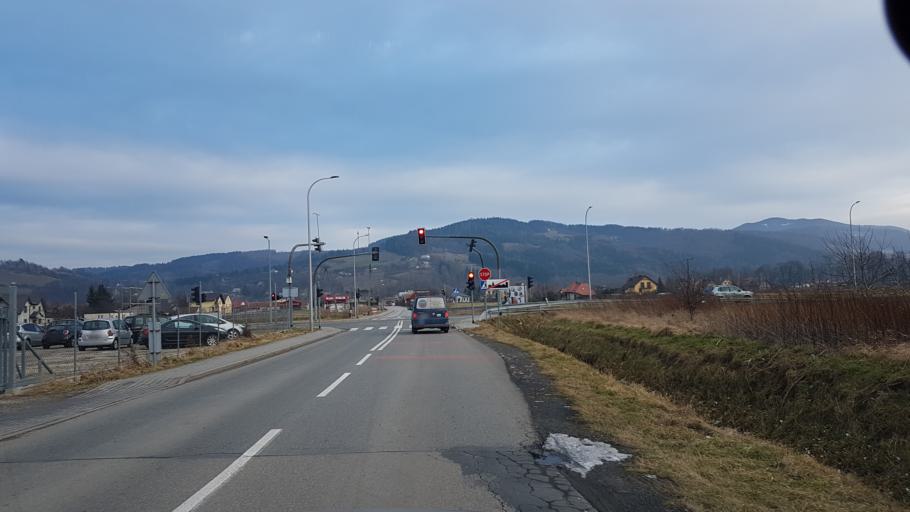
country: PL
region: Lesser Poland Voivodeship
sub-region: Powiat nowosadecki
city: Stary Sacz
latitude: 49.5415
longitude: 20.6465
